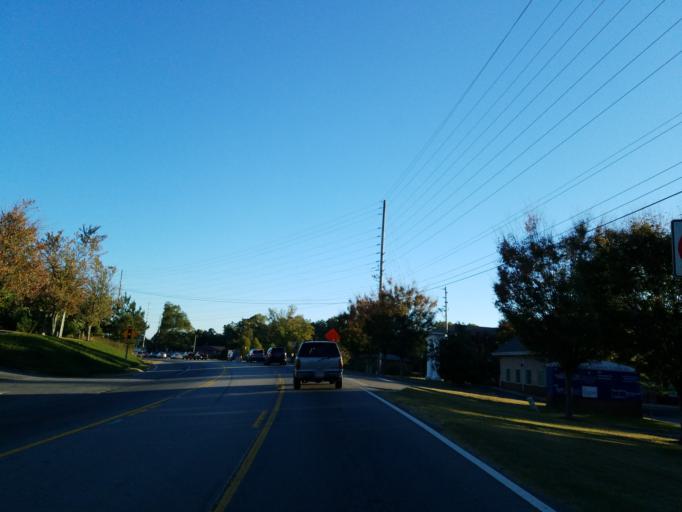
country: US
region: Georgia
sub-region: Dawson County
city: Dawsonville
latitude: 34.3694
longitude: -84.0420
